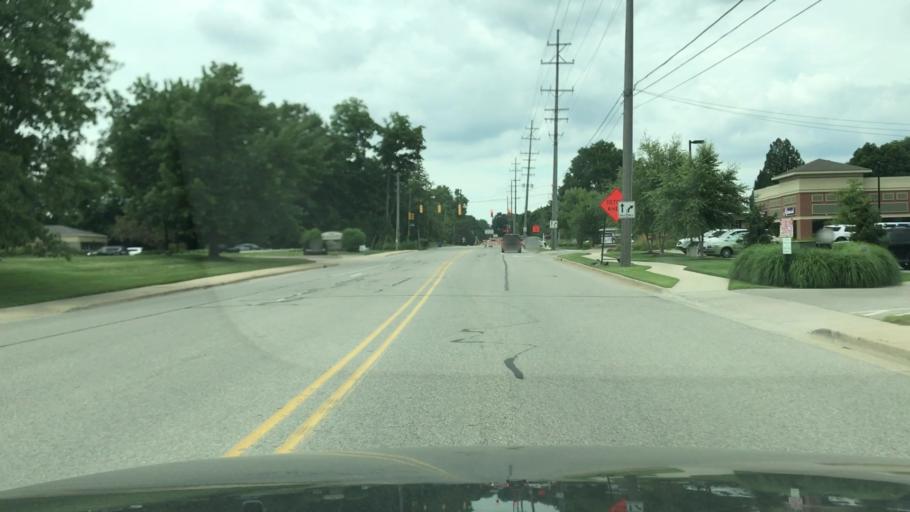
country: US
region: Michigan
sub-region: Kent County
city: East Grand Rapids
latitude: 42.9471
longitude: -85.5558
